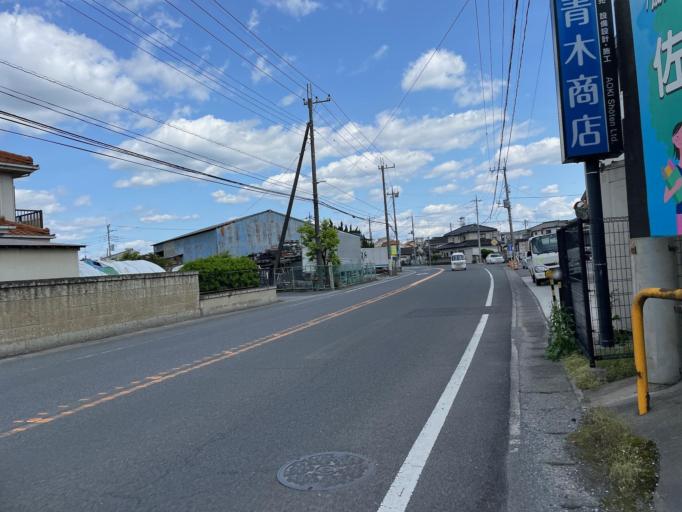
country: JP
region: Tochigi
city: Sano
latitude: 36.3190
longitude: 139.6441
